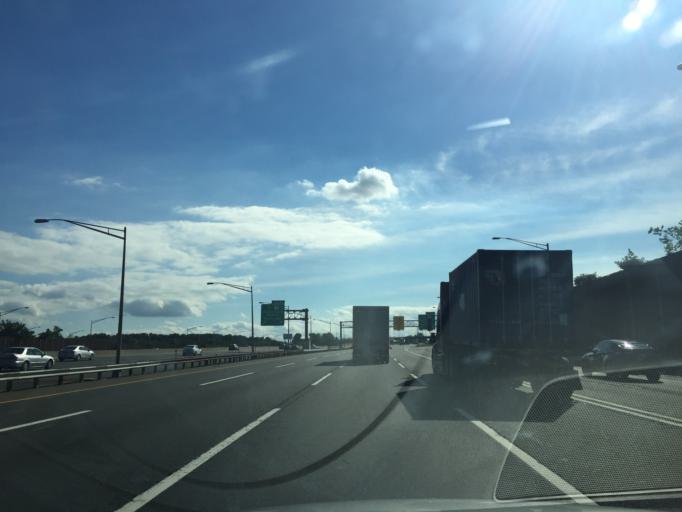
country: US
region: New Jersey
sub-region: Middlesex County
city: Woodbridge
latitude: 40.5474
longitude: -74.2817
